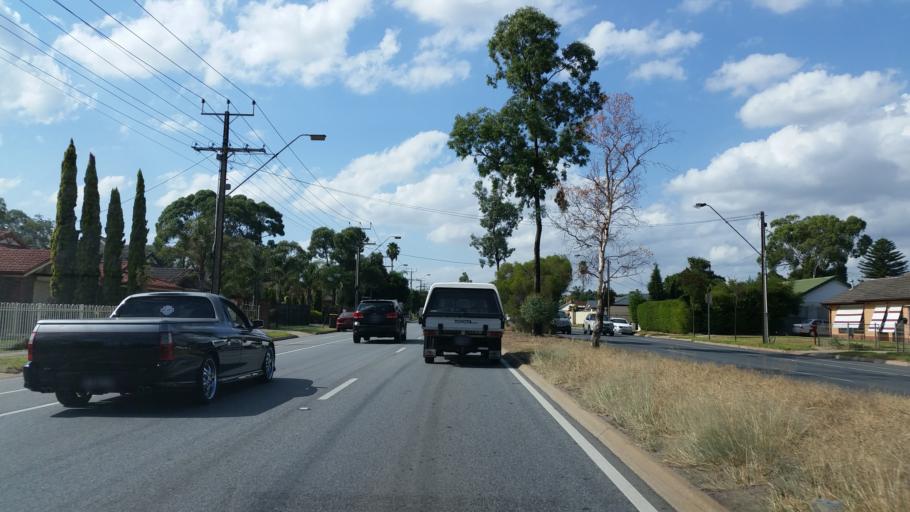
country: AU
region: South Australia
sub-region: Salisbury
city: Salisbury
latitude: -34.7951
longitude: 138.6121
